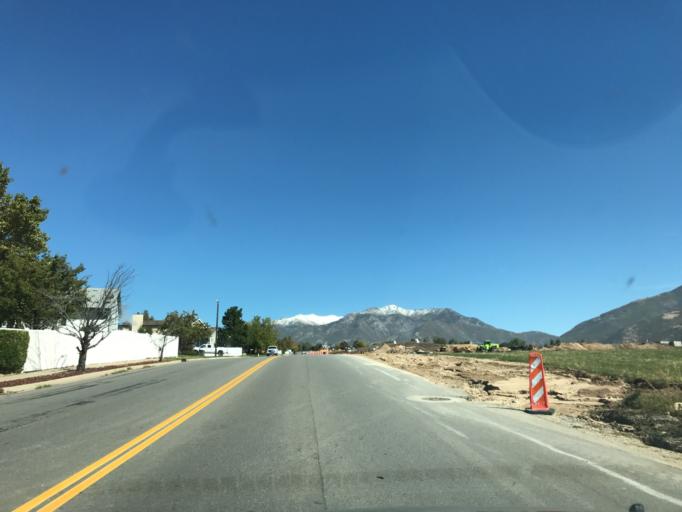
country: US
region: Utah
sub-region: Davis County
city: Hill Air Force Bace
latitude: 41.0913
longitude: -111.9433
